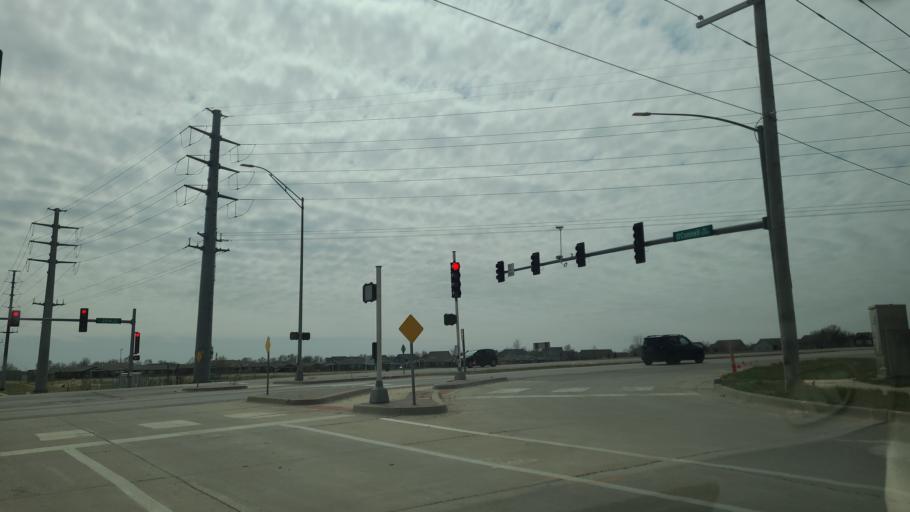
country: US
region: Kansas
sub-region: Douglas County
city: Lawrence
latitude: 38.9430
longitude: -95.2049
